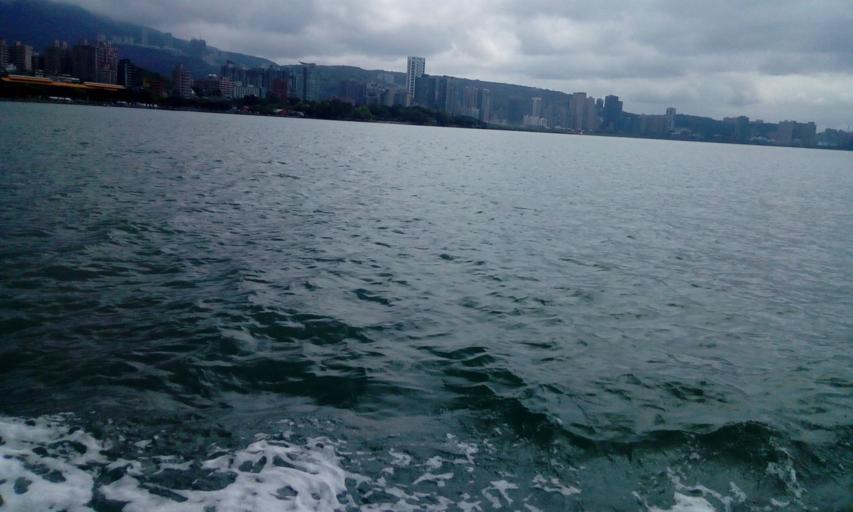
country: TW
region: Taipei
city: Taipei
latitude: 25.1676
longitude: 121.4380
